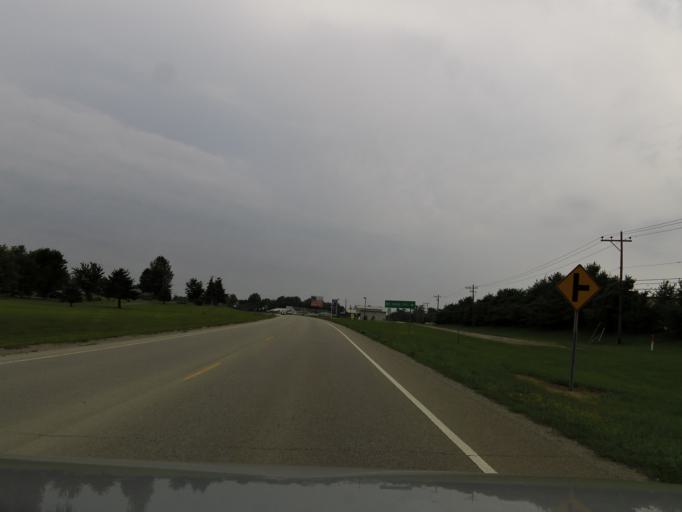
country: US
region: Ohio
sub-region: Brown County
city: Georgetown
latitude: 38.8996
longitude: -83.9019
